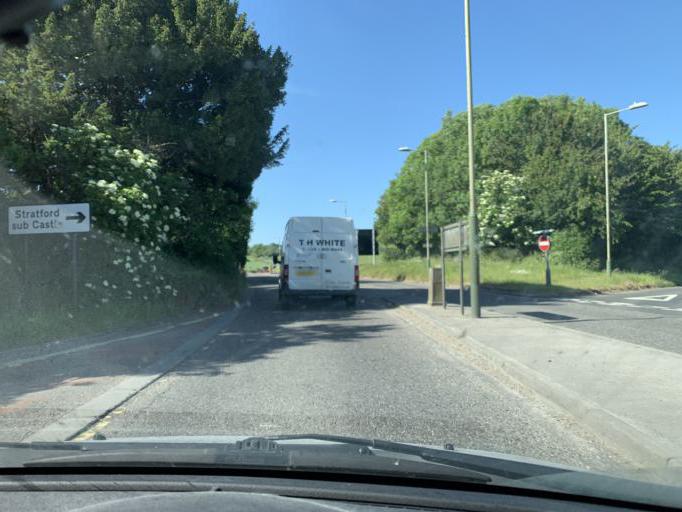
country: GB
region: England
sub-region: Wiltshire
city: Salisbury
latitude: 51.0985
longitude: -1.7967
